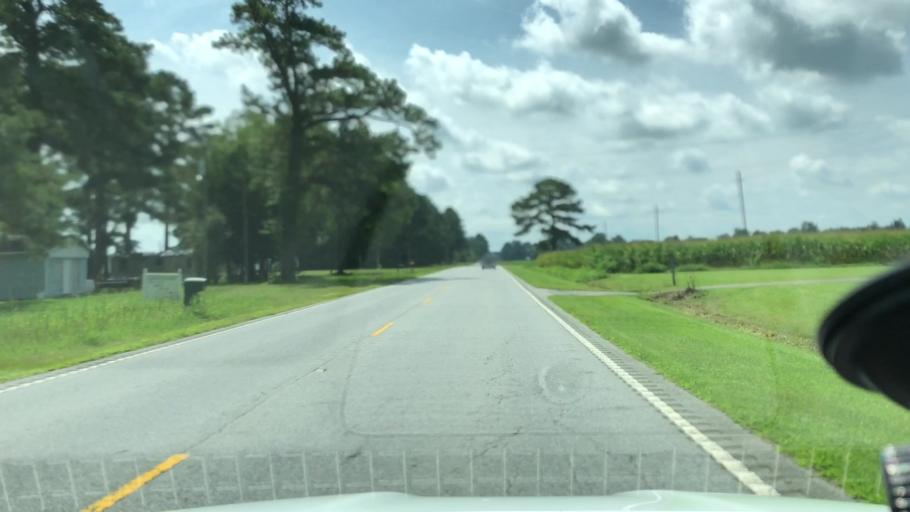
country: US
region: North Carolina
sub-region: Beaufort County
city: Washington
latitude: 35.6633
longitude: -77.0737
